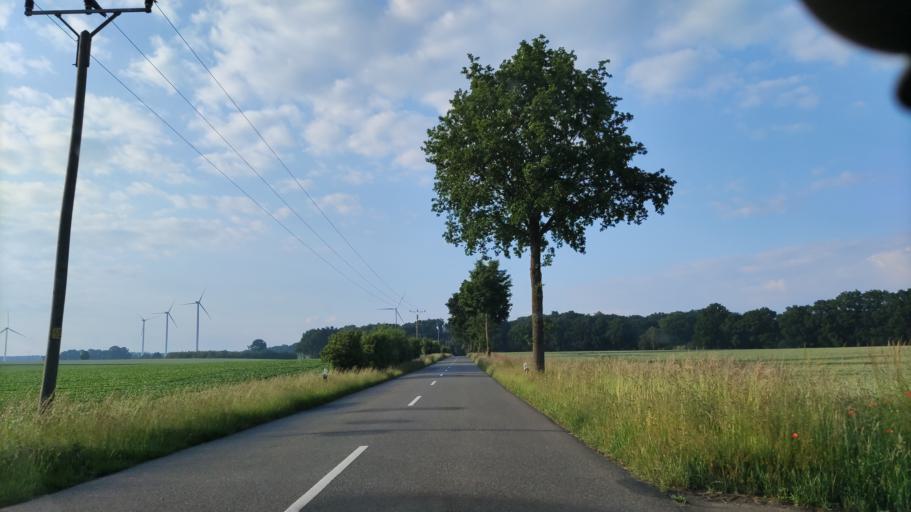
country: DE
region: Lower Saxony
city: Hanstedt Eins
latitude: 53.0364
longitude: 10.3474
